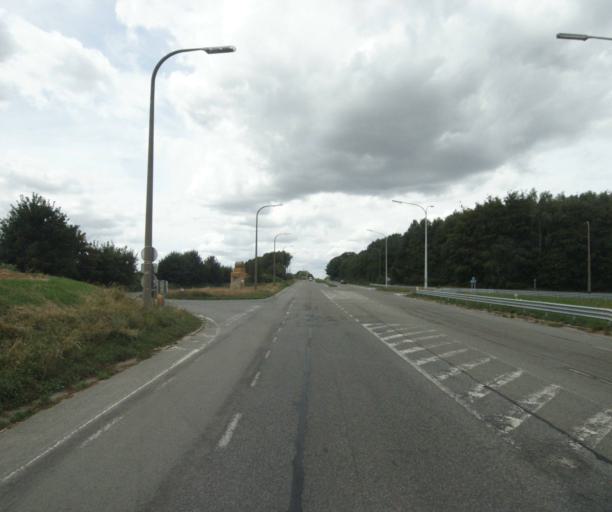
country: FR
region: Nord-Pas-de-Calais
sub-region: Departement du Nord
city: Camphin-en-Pevele
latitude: 50.6079
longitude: 3.3066
